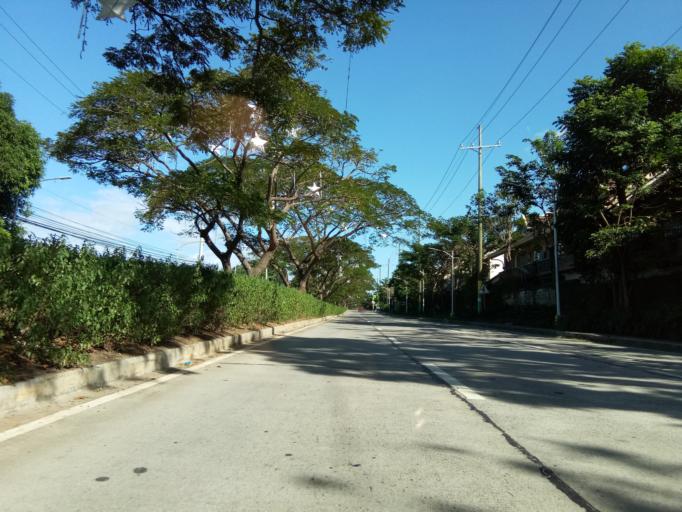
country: PH
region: Calabarzon
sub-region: Province of Cavite
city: Dasmarinas
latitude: 14.3509
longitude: 120.9594
